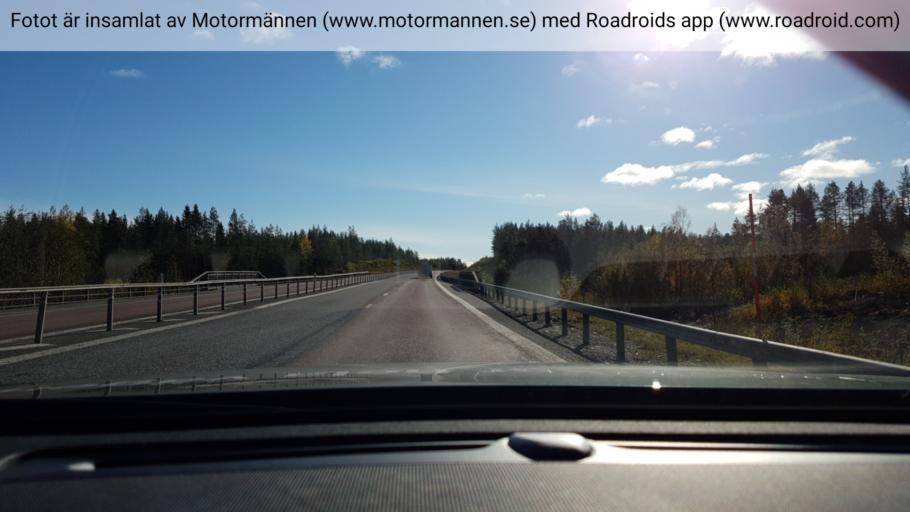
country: SE
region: Vaesterbotten
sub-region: Skelleftea Kommun
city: Soedra Bergsbyn
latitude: 64.6844
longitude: 21.0630
